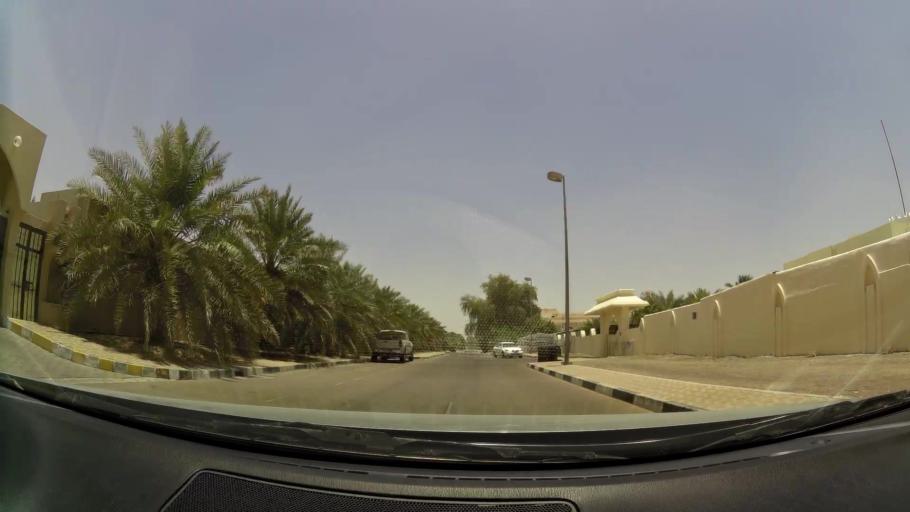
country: OM
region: Al Buraimi
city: Al Buraymi
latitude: 24.2697
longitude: 55.7228
